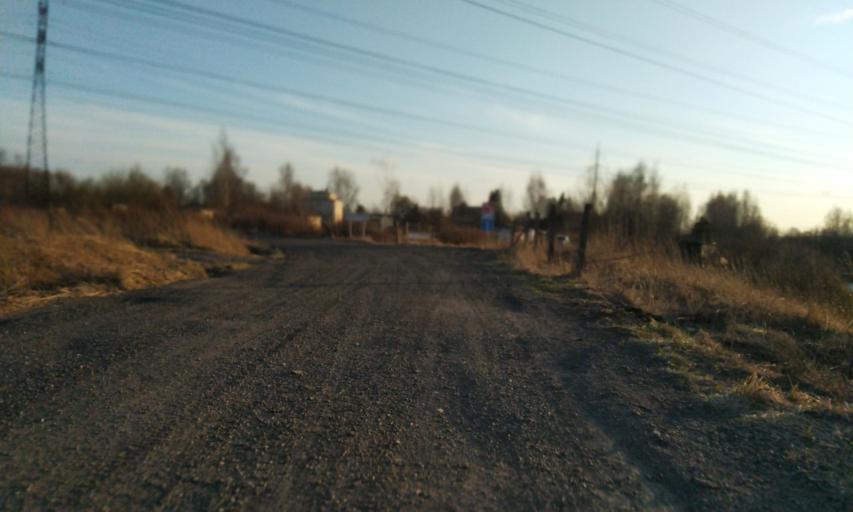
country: RU
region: Leningrad
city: Novoye Devyatkino
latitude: 60.0899
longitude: 30.4586
